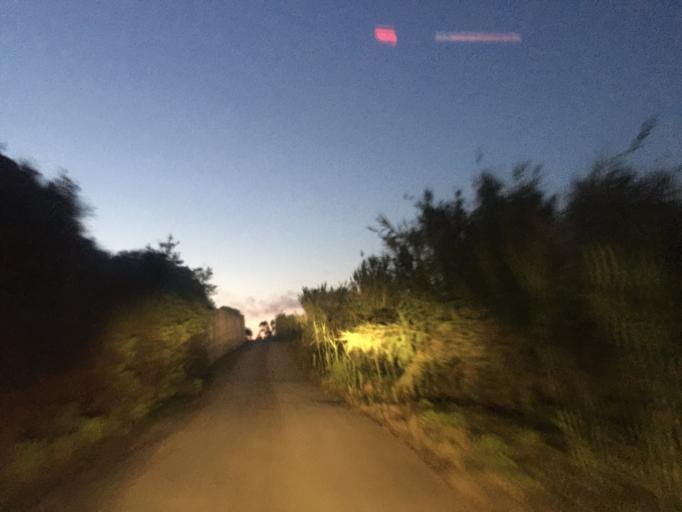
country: PT
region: Leiria
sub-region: Bombarral
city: Bombarral
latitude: 39.2916
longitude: -9.2237
